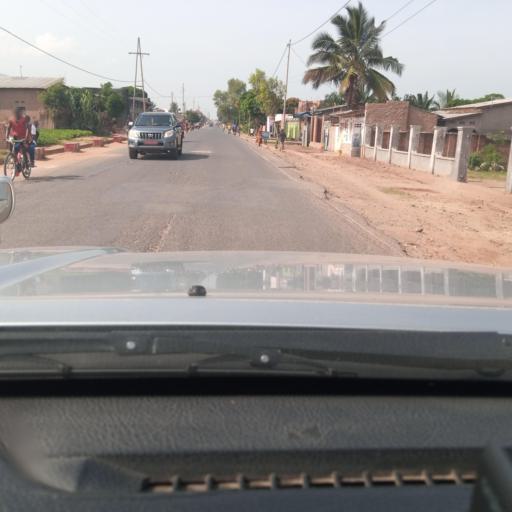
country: BI
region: Bujumbura Mairie
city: Bujumbura
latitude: -3.4575
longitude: 29.3511
